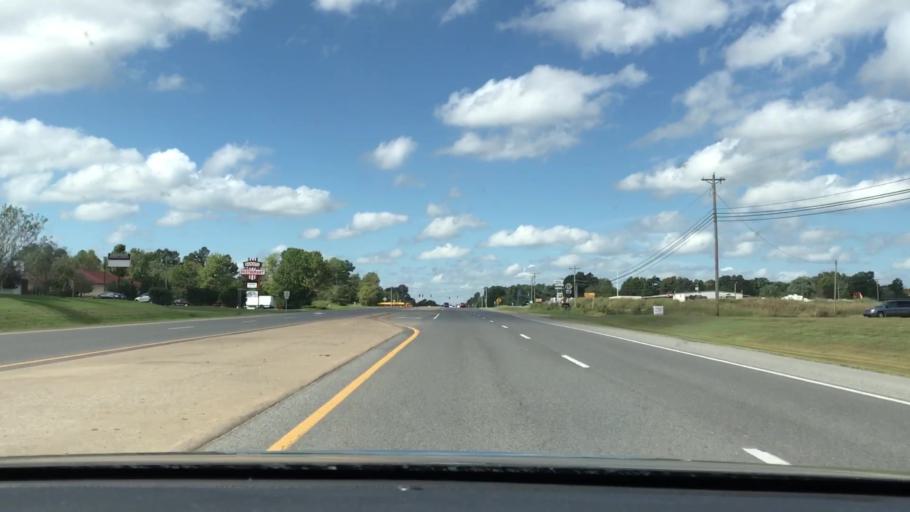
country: US
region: Kentucky
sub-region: McCracken County
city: Reidland
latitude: 37.0088
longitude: -88.5037
